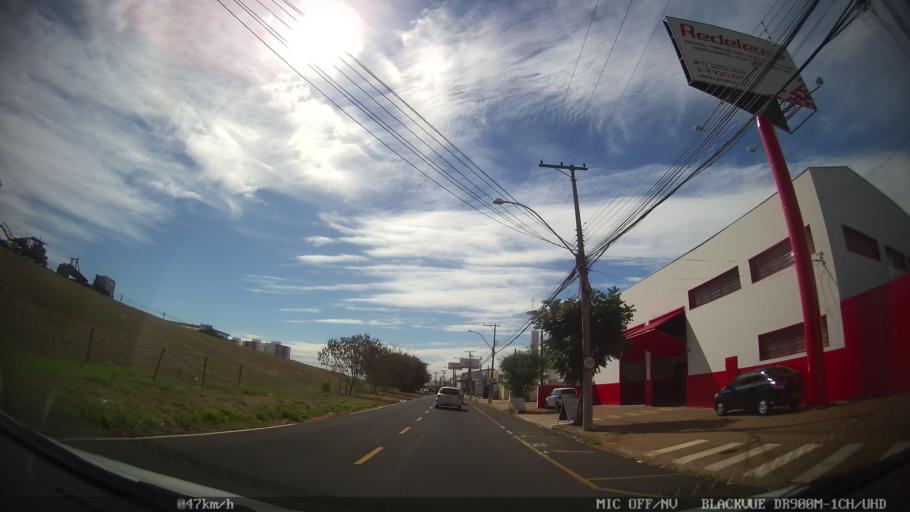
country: BR
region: Sao Paulo
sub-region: Sao Jose Do Rio Preto
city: Sao Jose do Rio Preto
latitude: -20.8252
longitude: -49.3578
